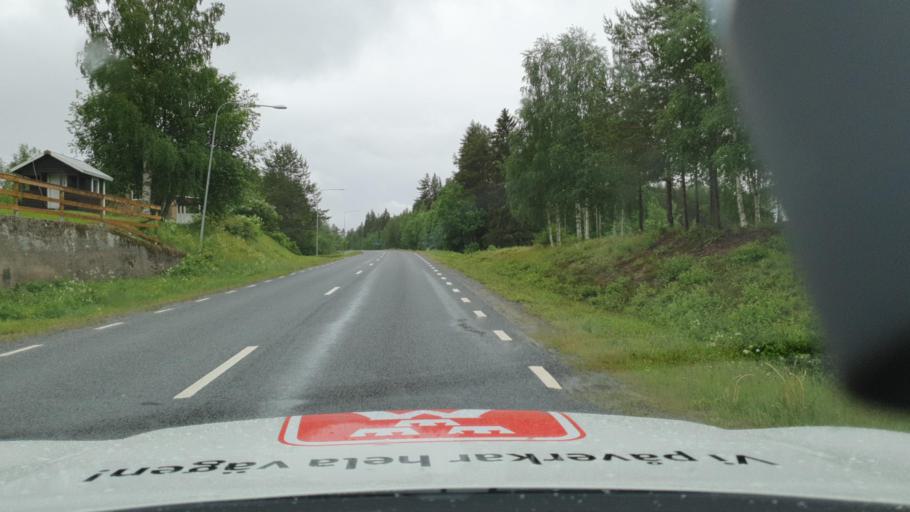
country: SE
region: Vaesterbotten
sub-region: Asele Kommun
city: Asele
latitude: 63.9345
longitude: 17.2726
